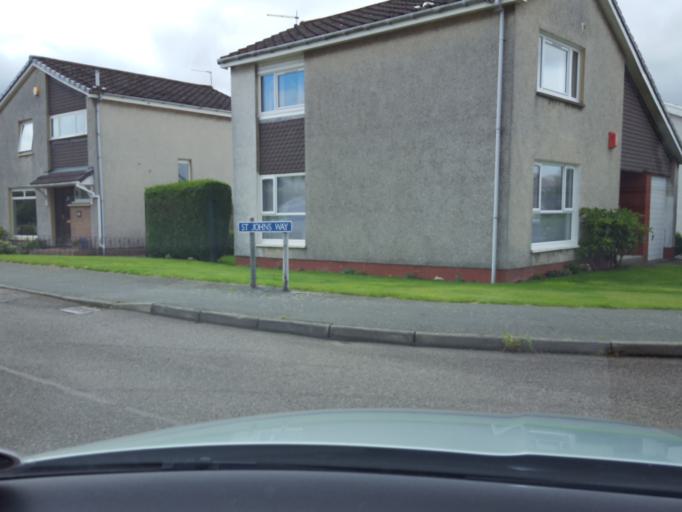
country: GB
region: Scotland
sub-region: Falkirk
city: Bo'ness
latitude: 56.0048
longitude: -3.6078
